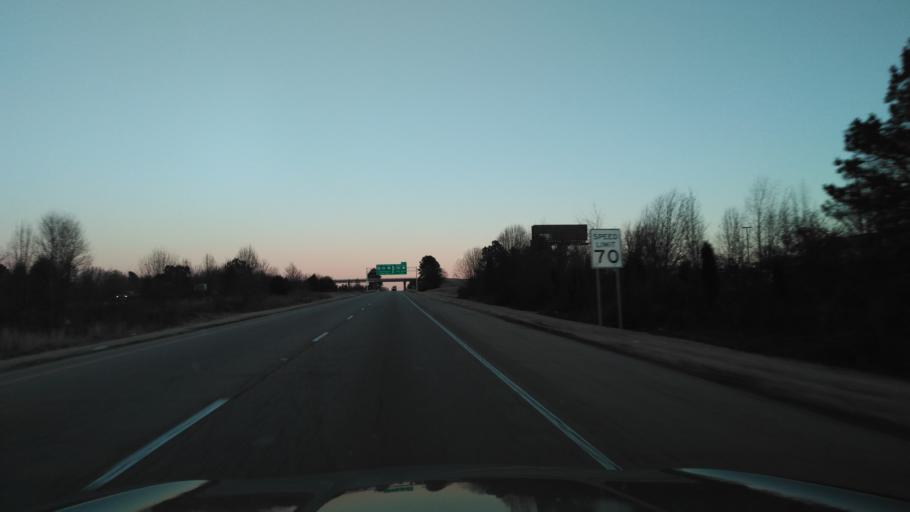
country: US
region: Arkansas
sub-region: Crawford County
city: Van Buren
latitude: 35.4614
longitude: -94.3462
